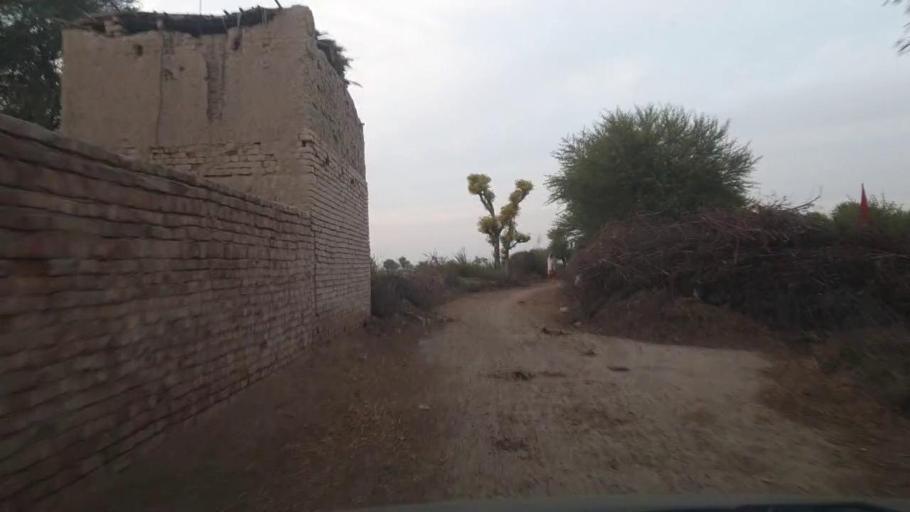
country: PK
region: Sindh
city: Shahpur Chakar
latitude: 26.0701
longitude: 68.5359
